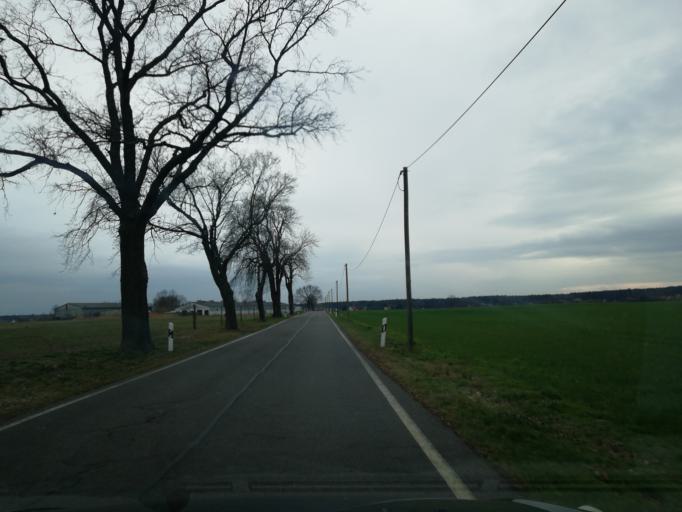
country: DE
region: Brandenburg
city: Calau
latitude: 51.7380
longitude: 14.0221
